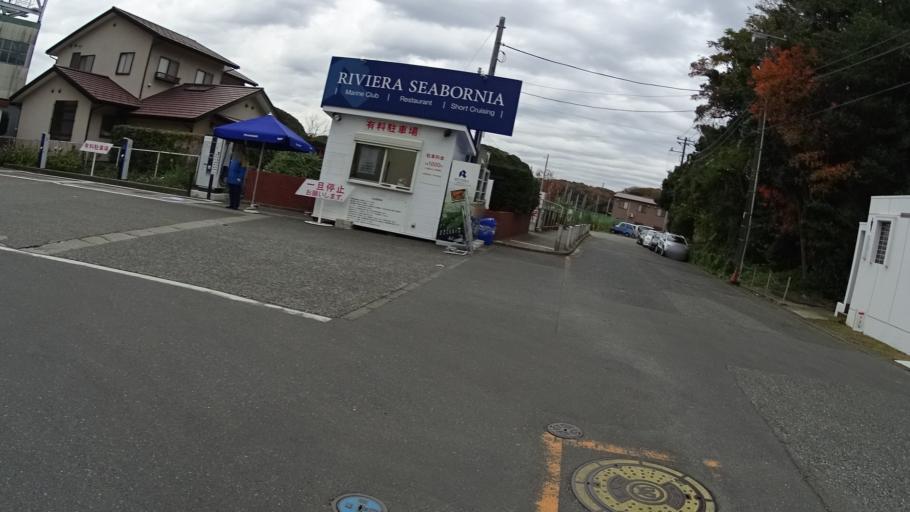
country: JP
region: Kanagawa
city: Miura
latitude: 35.1623
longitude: 139.6223
